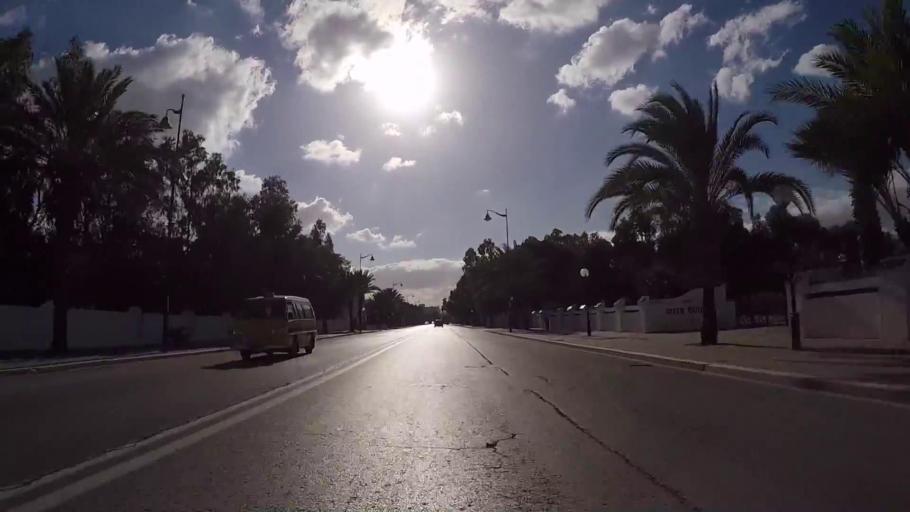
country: TN
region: Nabul
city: Al Hammamat
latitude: 36.3750
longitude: 10.5409
